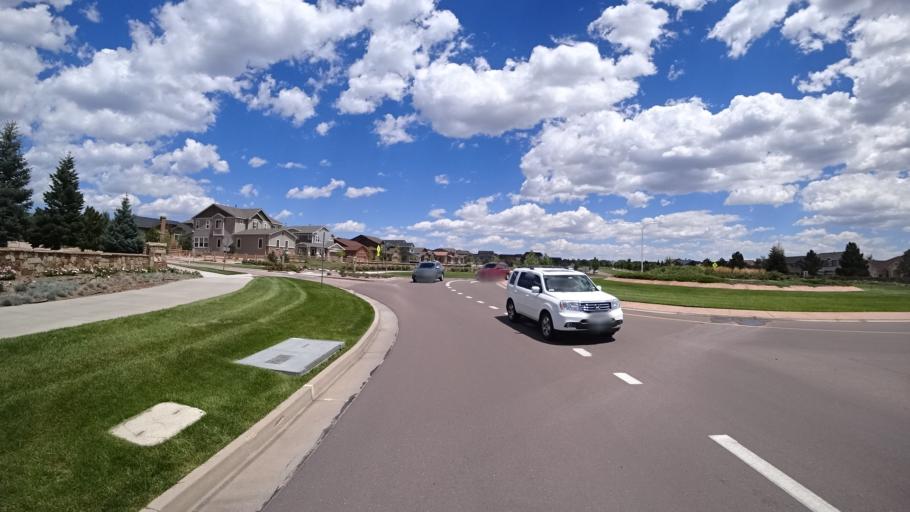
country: US
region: Colorado
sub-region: El Paso County
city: Black Forest
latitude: 38.9613
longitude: -104.7184
